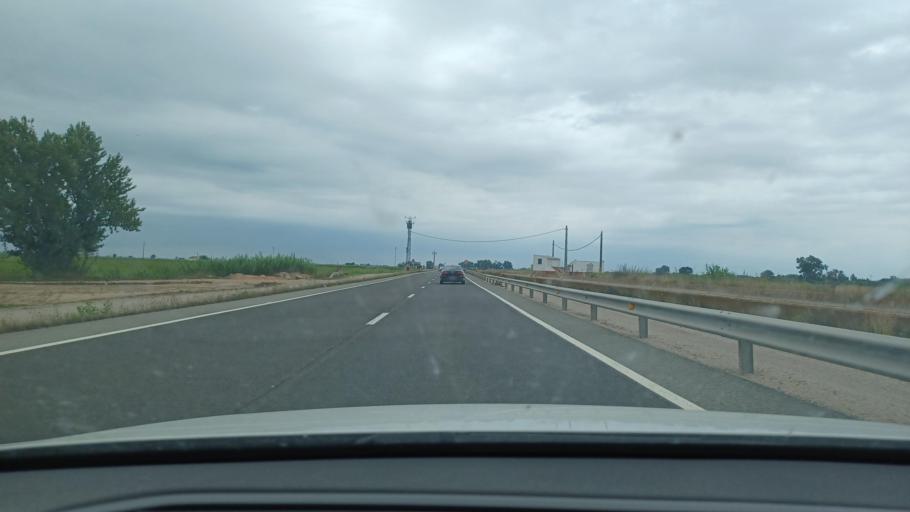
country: ES
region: Catalonia
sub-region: Provincia de Tarragona
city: Amposta
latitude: 40.7166
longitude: 0.6340
